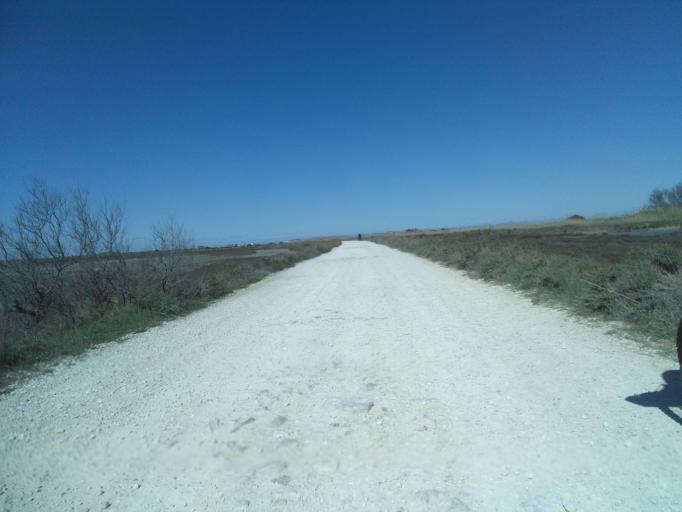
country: FR
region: Provence-Alpes-Cote d'Azur
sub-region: Departement des Bouches-du-Rhone
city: Saintes-Maries-de-la-Mer
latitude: 43.4532
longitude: 4.5874
